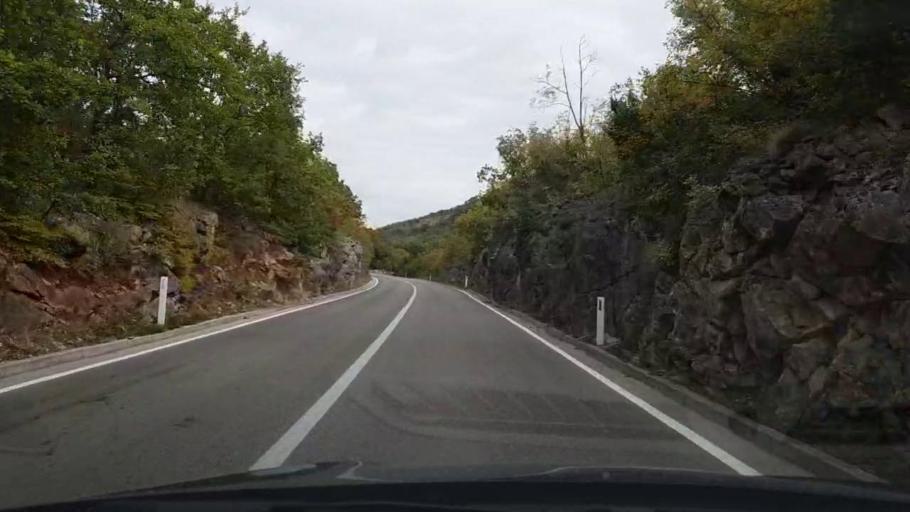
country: BA
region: Republika Srpska
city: Trebinje
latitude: 42.6879
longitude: 18.2659
